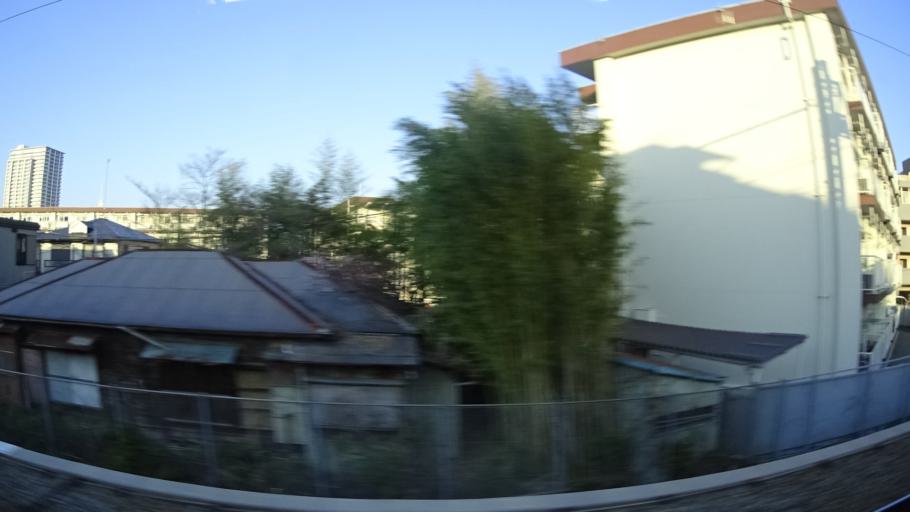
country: JP
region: Kanagawa
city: Yokohama
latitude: 35.3816
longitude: 139.6168
